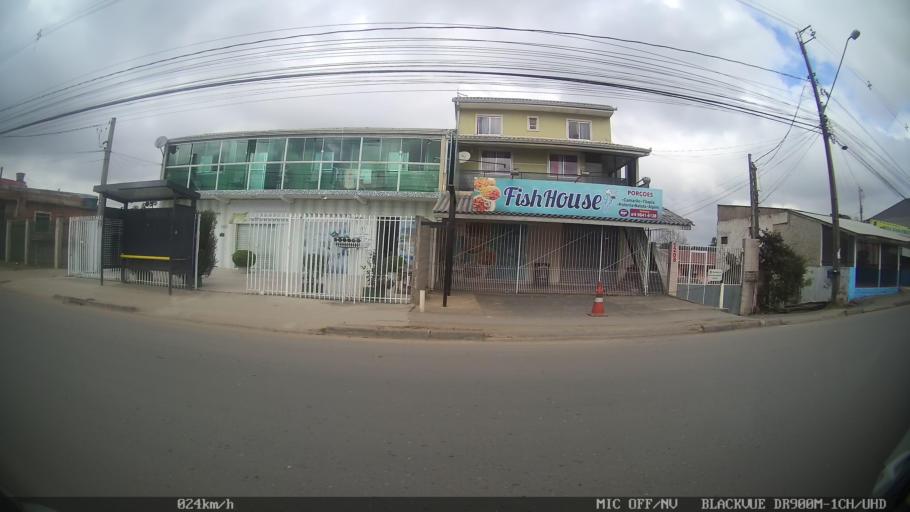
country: BR
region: Parana
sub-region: Colombo
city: Colombo
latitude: -25.3458
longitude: -49.2443
